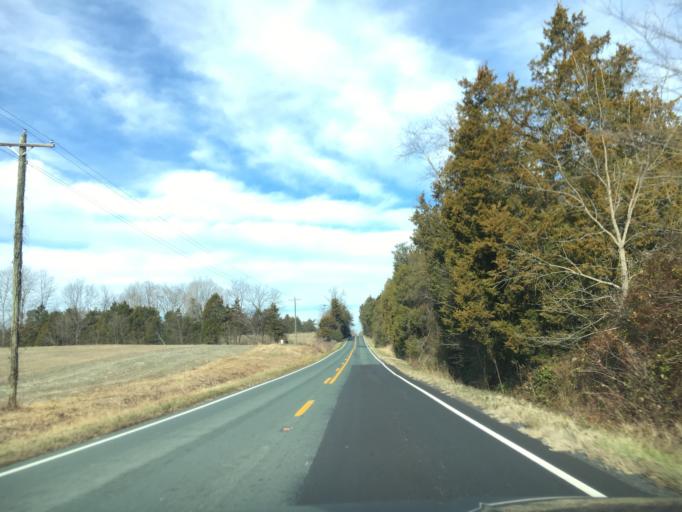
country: US
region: Virginia
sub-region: Louisa County
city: Louisa
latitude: 38.1726
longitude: -77.9370
